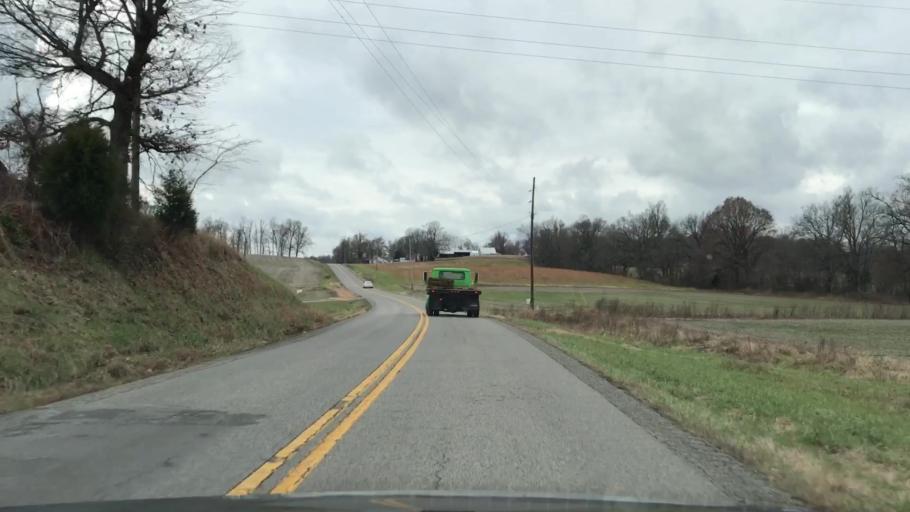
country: US
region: Kentucky
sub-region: Webster County
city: Sebree
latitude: 37.4934
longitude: -87.4565
